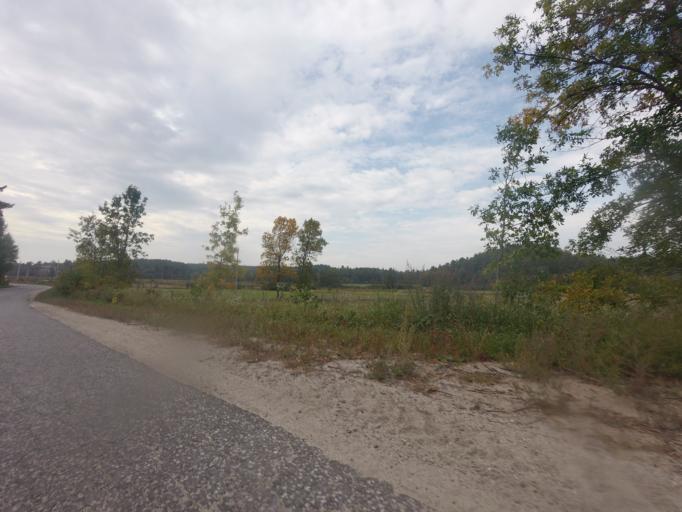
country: CA
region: Quebec
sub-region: Outaouais
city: Wakefield
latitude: 45.9791
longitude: -75.9343
